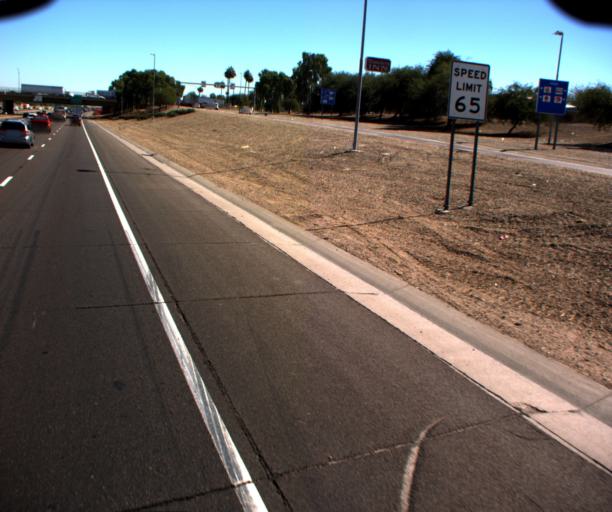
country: US
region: Arizona
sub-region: Maricopa County
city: Glendale
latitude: 33.4626
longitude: -112.1719
